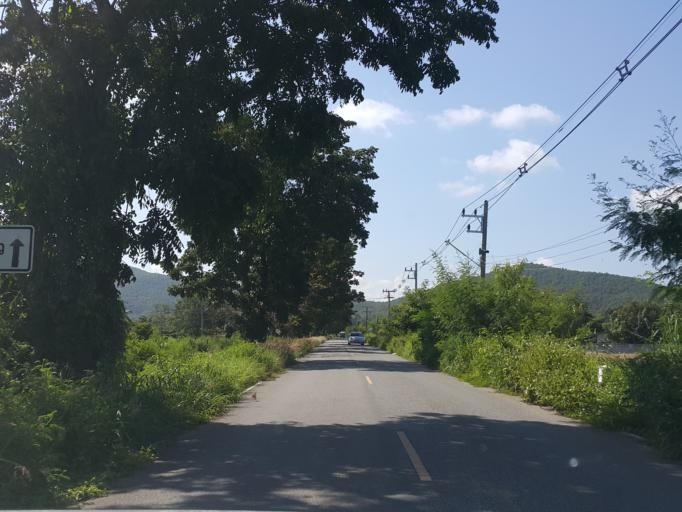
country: TH
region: Chiang Mai
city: Mae On
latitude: 18.7867
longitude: 99.1833
